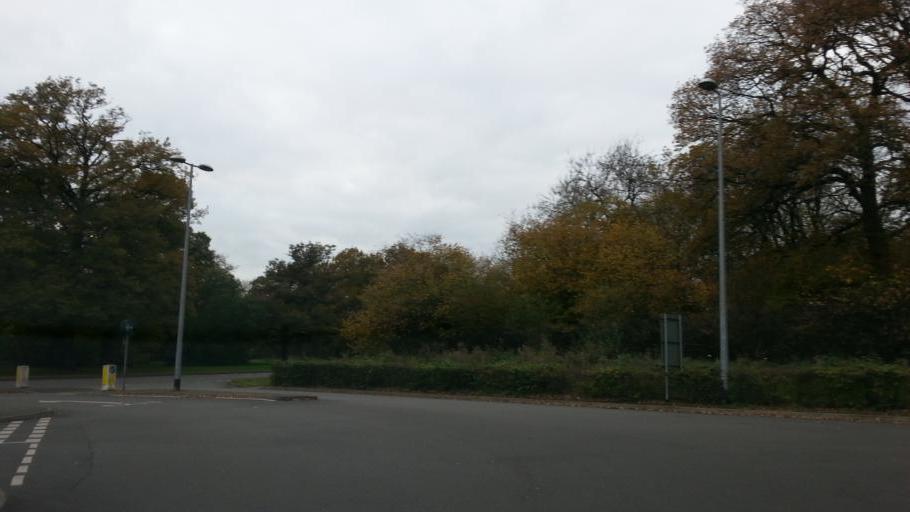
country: GB
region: England
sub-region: Northamptonshire
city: Corby
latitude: 52.4872
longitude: -0.7062
